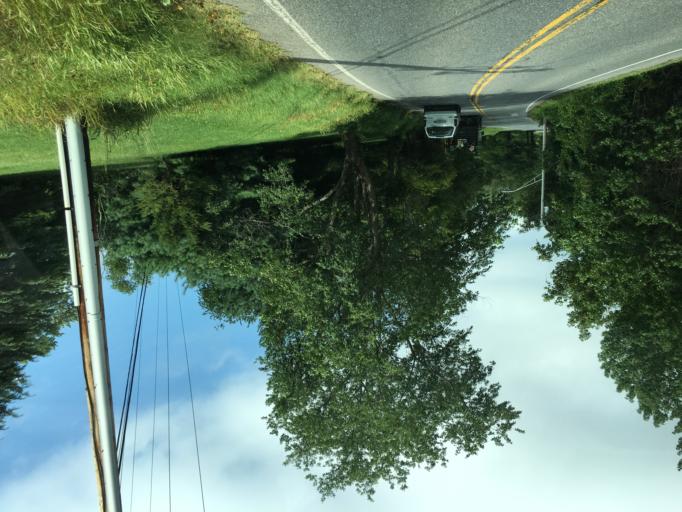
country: US
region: Maryland
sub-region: Anne Arundel County
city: Crownsville
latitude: 39.0171
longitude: -76.5960
